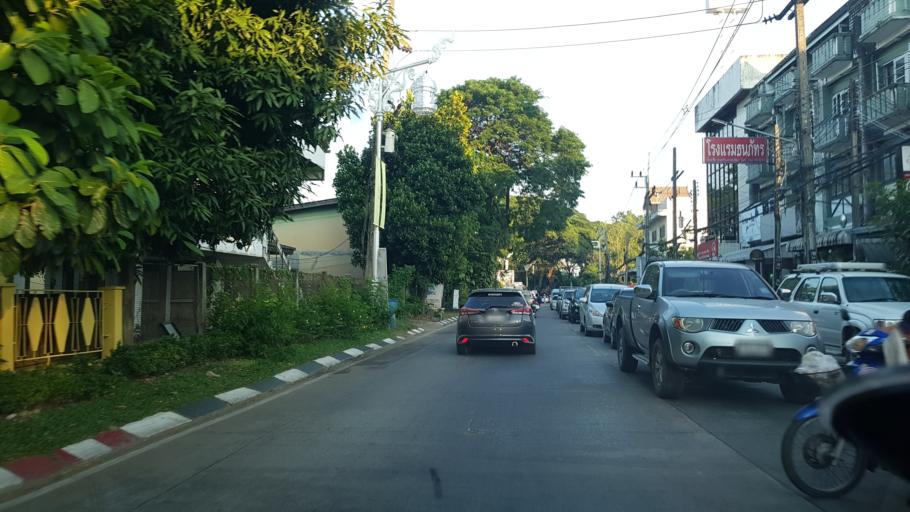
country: TH
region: Chiang Rai
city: Chiang Rai
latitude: 19.9128
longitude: 99.8332
